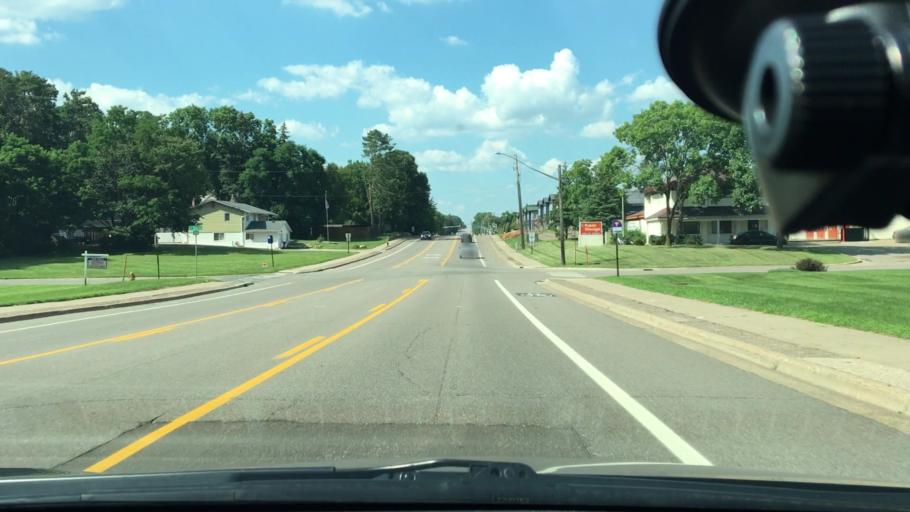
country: US
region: Minnesota
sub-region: Hennepin County
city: Golden Valley
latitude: 45.0032
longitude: -93.3803
